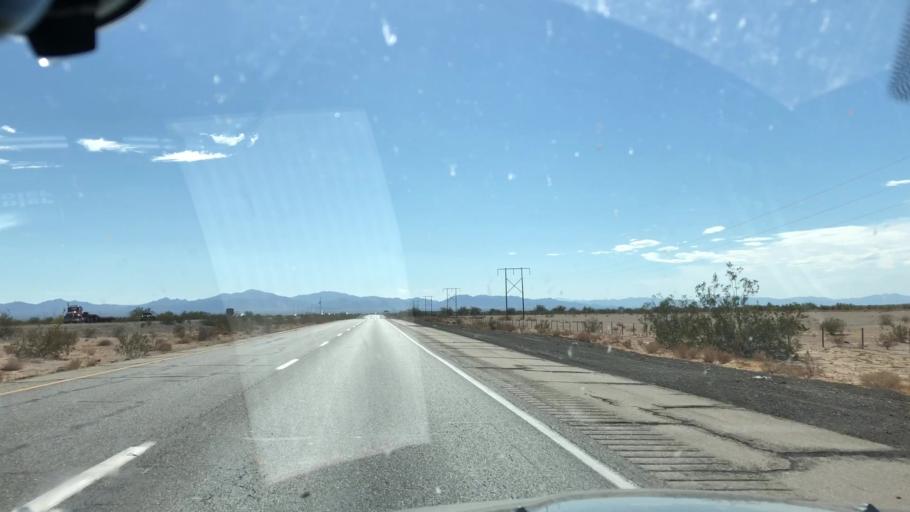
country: US
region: California
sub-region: Riverside County
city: Mesa Verde
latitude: 33.6063
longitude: -114.9657
